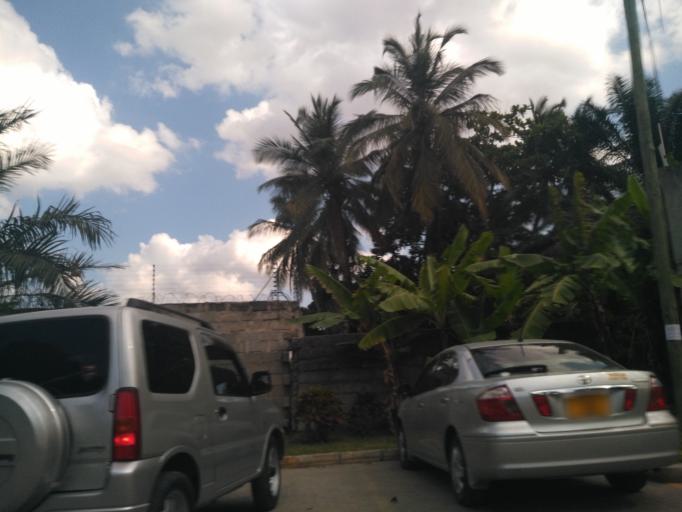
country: TZ
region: Dar es Salaam
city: Magomeni
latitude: -6.7774
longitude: 39.2565
